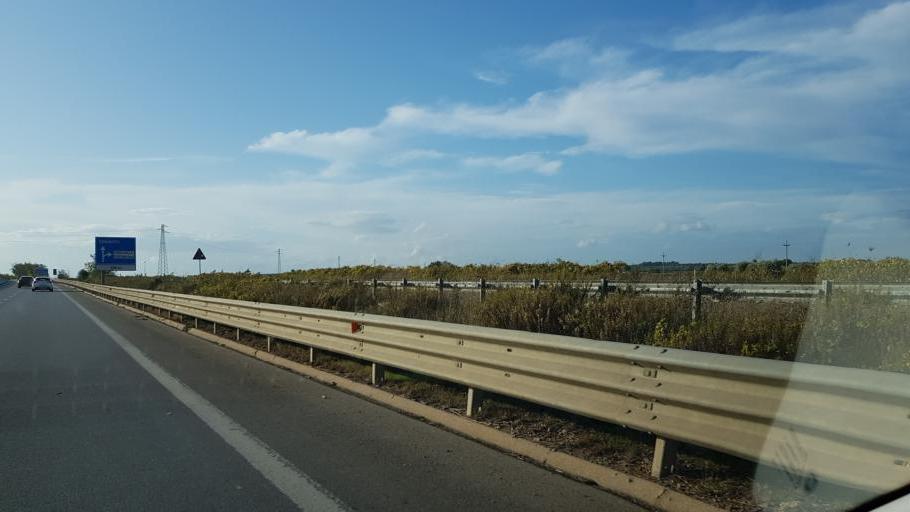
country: IT
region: Apulia
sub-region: Provincia di Brindisi
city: Francavilla Fontana
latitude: 40.5464
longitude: 17.5842
